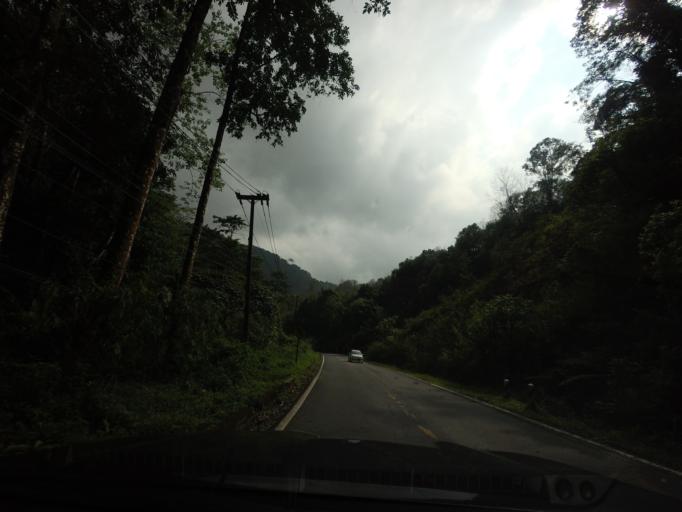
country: TH
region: Nan
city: Bo Kluea
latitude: 19.1911
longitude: 101.0767
